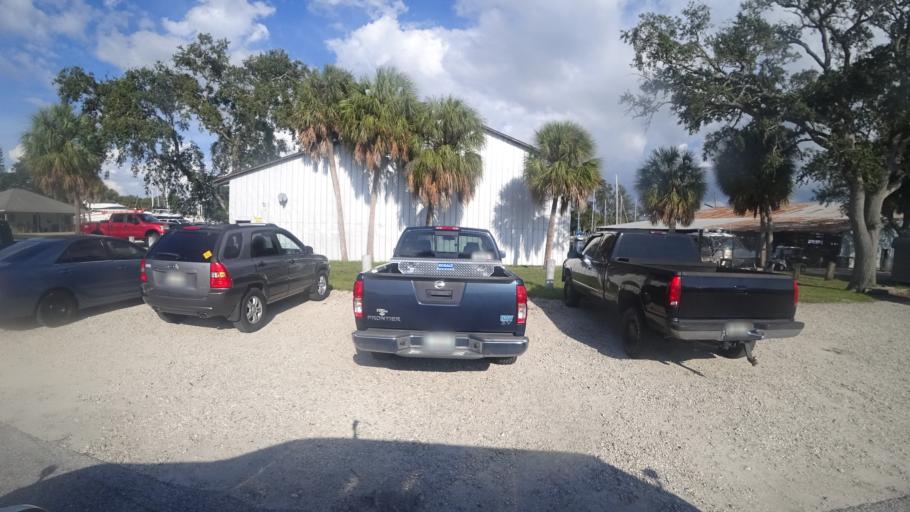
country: US
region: Florida
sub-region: Manatee County
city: West Bradenton
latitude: 27.5244
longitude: -82.6212
